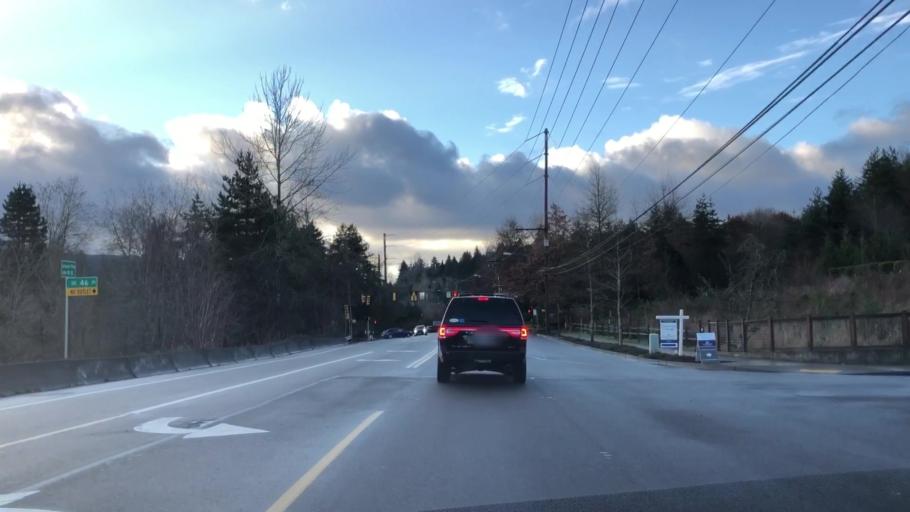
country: US
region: Washington
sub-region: King County
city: Issaquah
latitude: 47.5624
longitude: -122.0250
